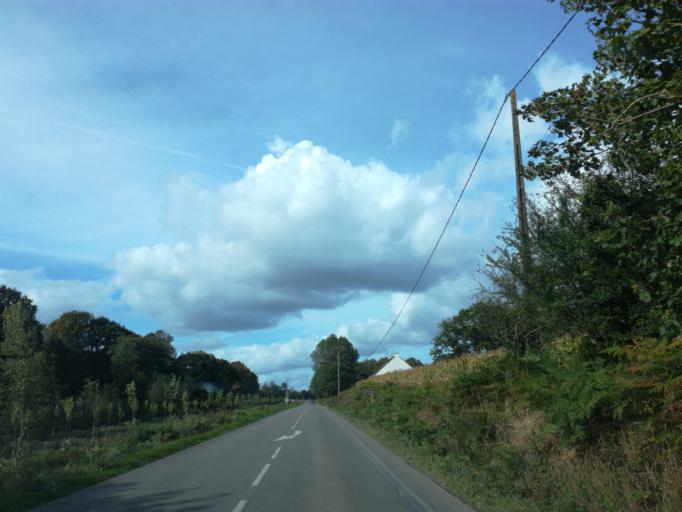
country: FR
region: Brittany
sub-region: Departement du Morbihan
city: Rohan
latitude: 48.0756
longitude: -2.7563
